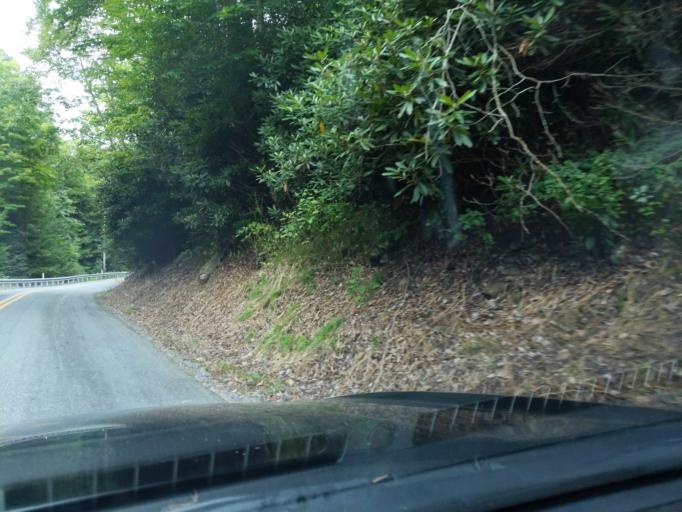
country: US
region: Pennsylvania
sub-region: Cambria County
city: Portage
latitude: 40.3360
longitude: -78.5820
